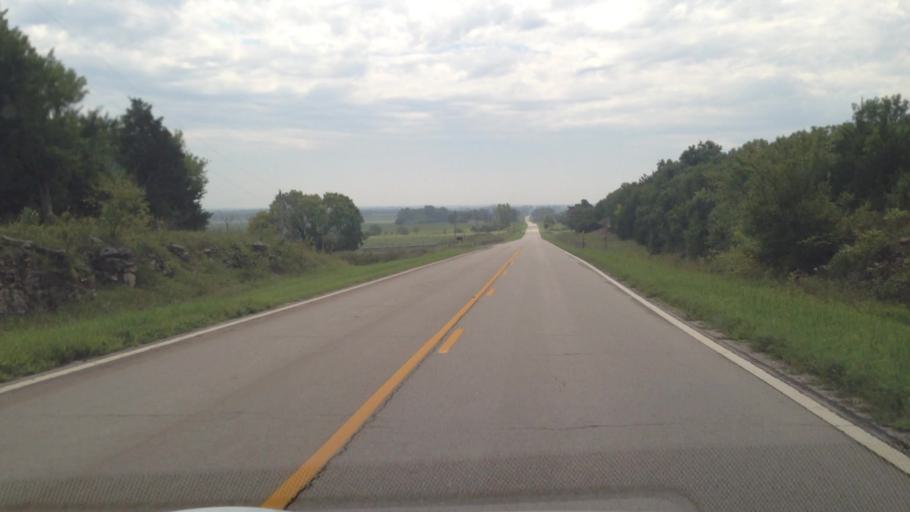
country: US
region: Kansas
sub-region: Bourbon County
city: Fort Scott
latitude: 37.8237
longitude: -94.9790
